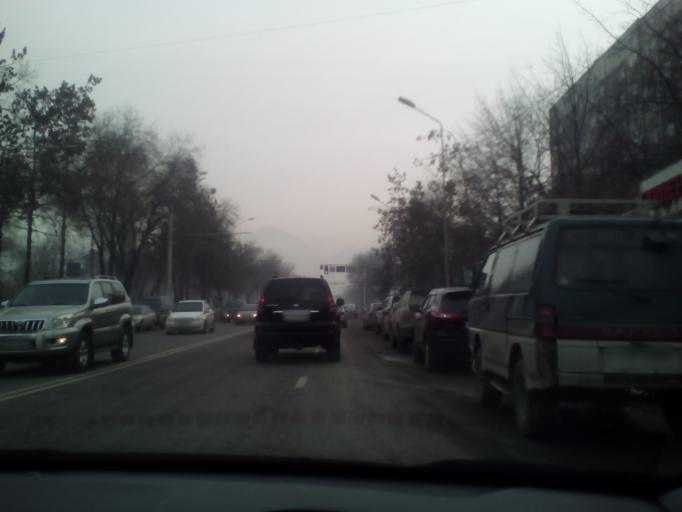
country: KZ
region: Almaty Qalasy
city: Almaty
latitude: 43.2343
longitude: 76.8316
